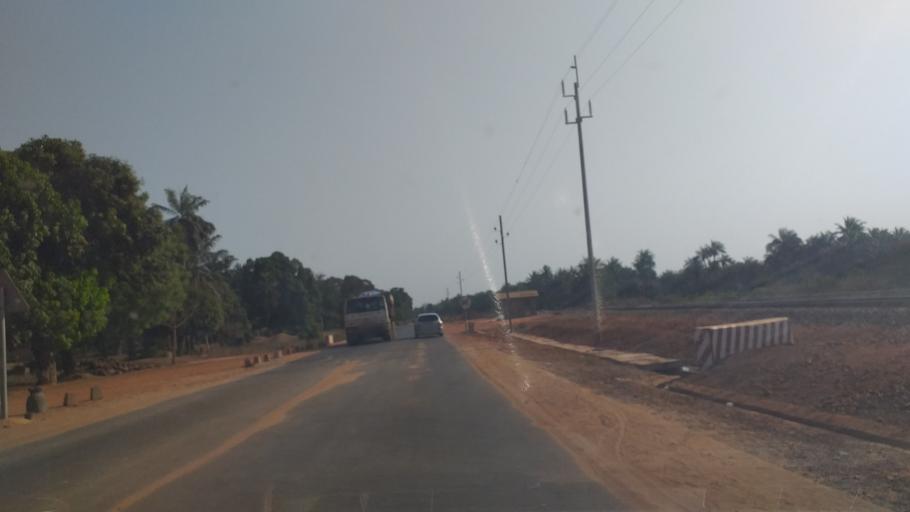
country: GN
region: Boke
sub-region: Boke Prefecture
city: Kamsar
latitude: 10.7391
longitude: -14.5143
